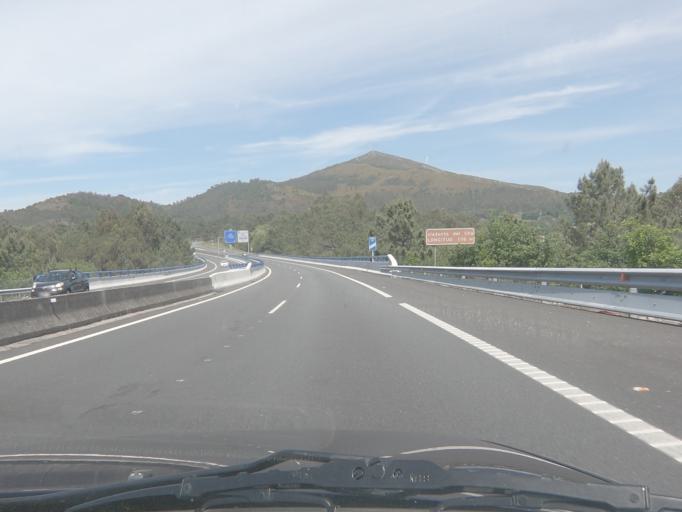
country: ES
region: Galicia
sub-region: Provincia da Coruna
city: Padron
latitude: 42.7292
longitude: -8.6362
